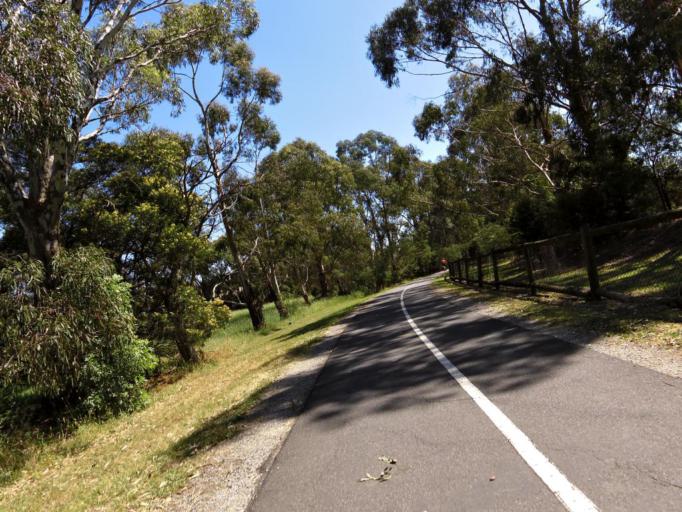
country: AU
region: Victoria
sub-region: Knox
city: Ferntree Gully
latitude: -37.8896
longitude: 145.2819
